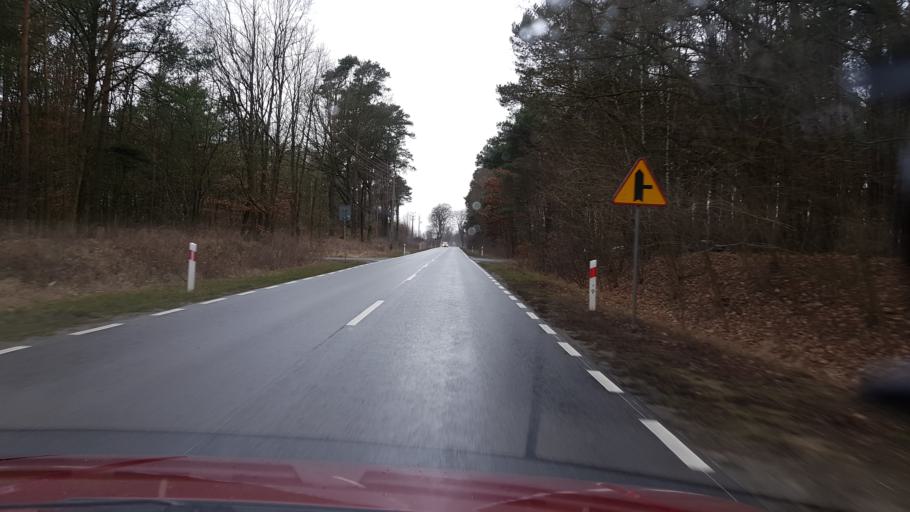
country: PL
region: West Pomeranian Voivodeship
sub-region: Powiat gryfinski
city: Gryfino
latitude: 53.2567
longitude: 14.5288
